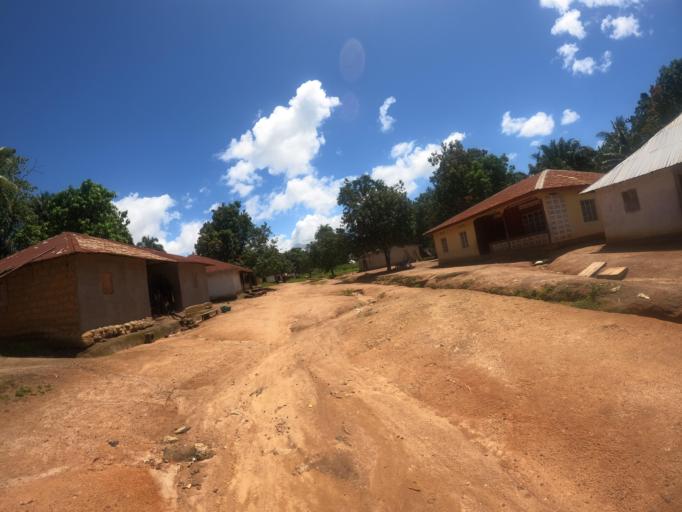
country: SL
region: Northern Province
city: Makeni
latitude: 8.8498
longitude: -12.1147
